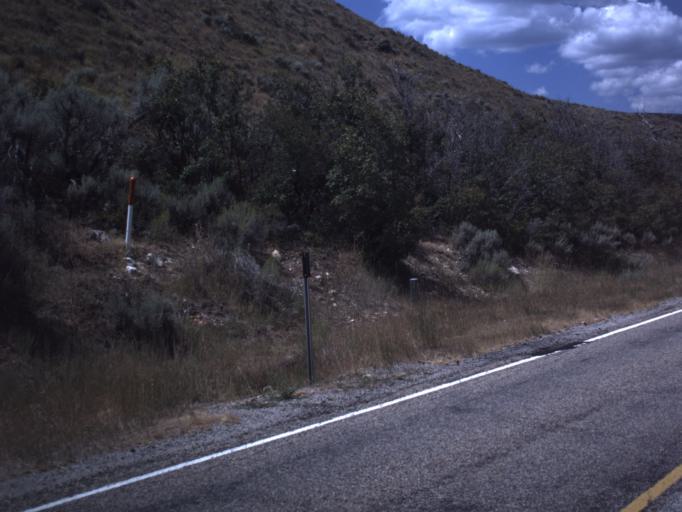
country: US
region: Utah
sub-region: Rich County
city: Randolph
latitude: 41.8493
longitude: -111.3550
